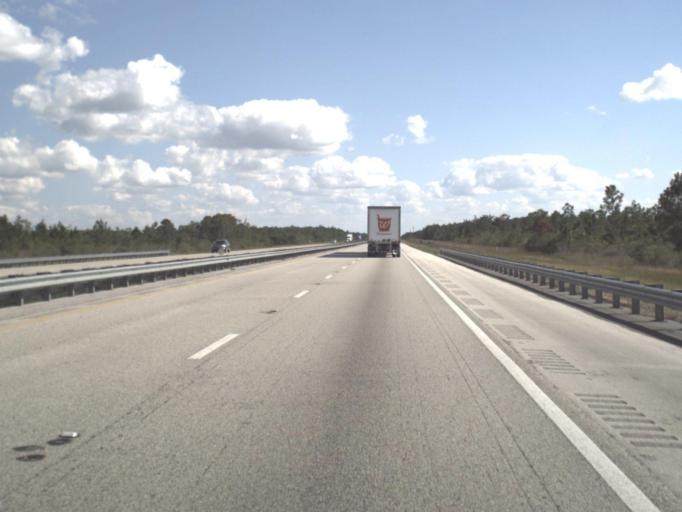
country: US
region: Florida
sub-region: Osceola County
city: Saint Cloud
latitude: 27.9934
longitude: -81.1314
